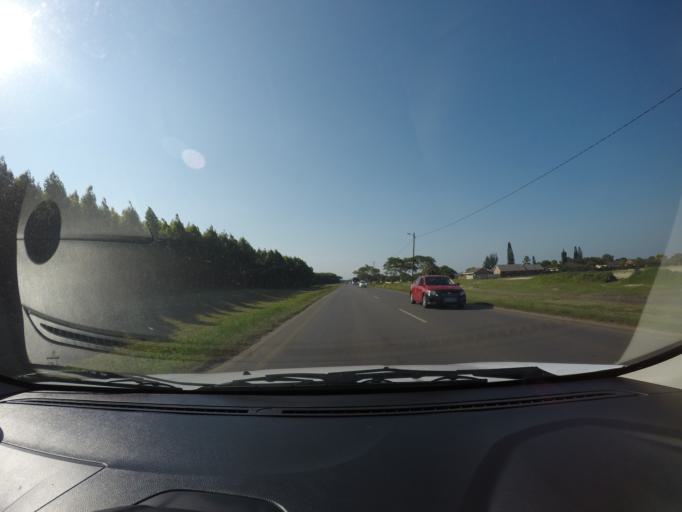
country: ZA
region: KwaZulu-Natal
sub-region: uThungulu District Municipality
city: Richards Bay
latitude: -28.7199
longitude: 32.0330
